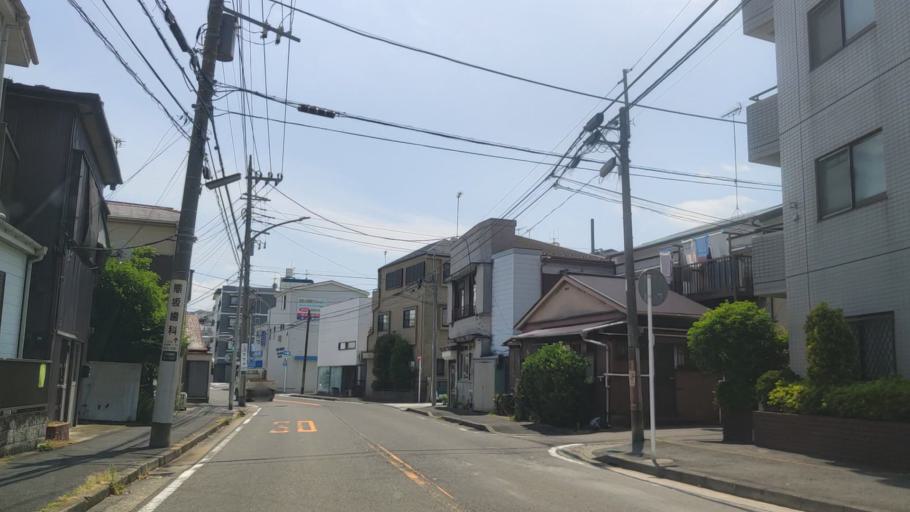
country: JP
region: Kanagawa
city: Yokohama
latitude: 35.4337
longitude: 139.6575
